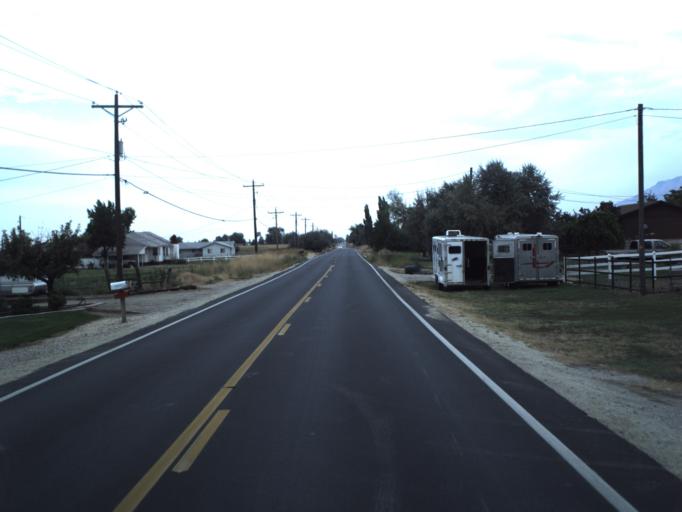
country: US
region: Utah
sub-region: Weber County
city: West Haven
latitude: 41.2143
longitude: -112.0929
